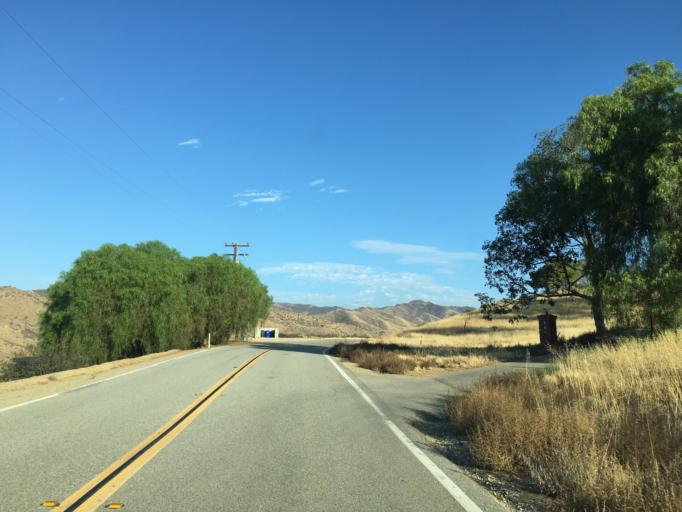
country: US
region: California
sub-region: Los Angeles County
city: Castaic
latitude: 34.5168
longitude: -118.6345
